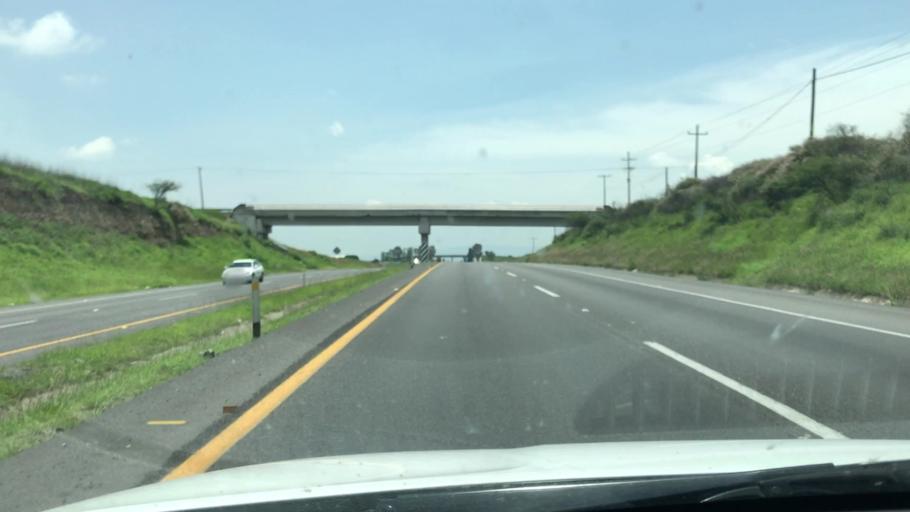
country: MX
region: Guanajuato
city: Penjamo
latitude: 20.3841
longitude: -101.7932
